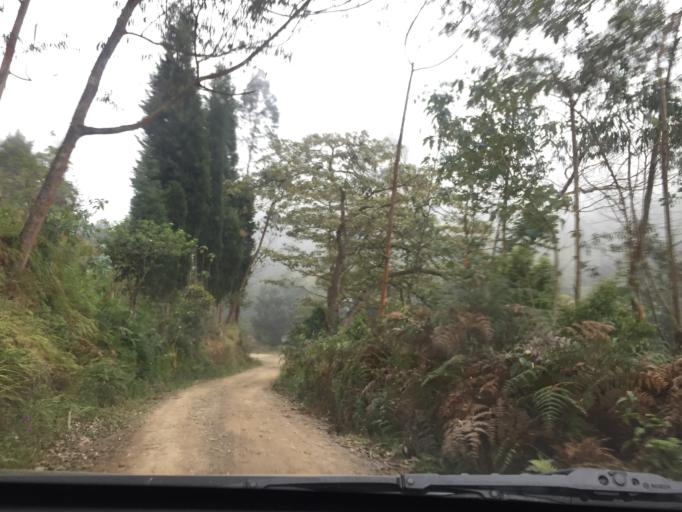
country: CO
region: Cundinamarca
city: Bojaca
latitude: 4.7065
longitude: -74.3649
